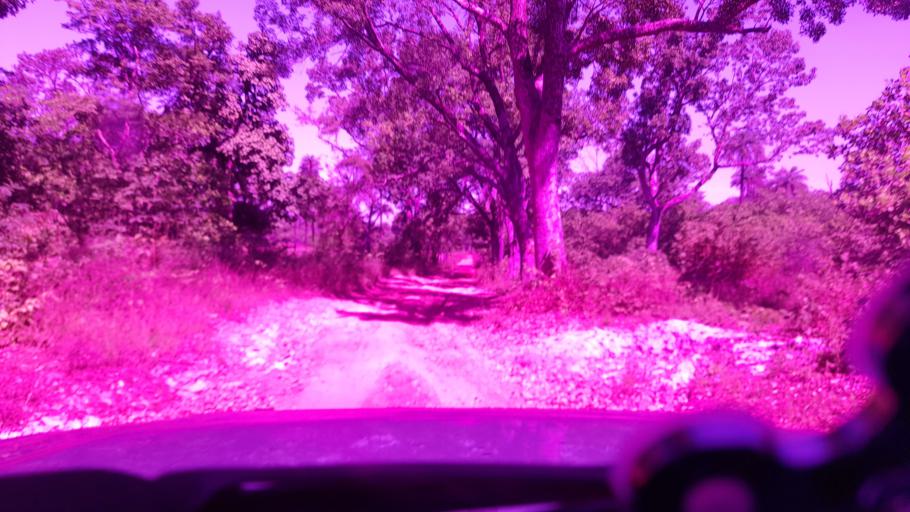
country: GW
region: Oio
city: Bissora
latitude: 12.4290
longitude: -15.5747
